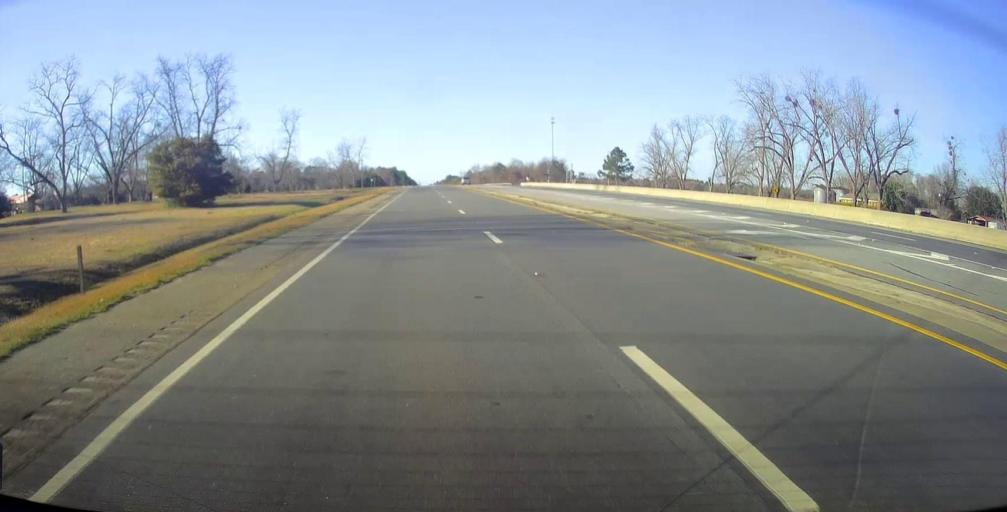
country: US
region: Georgia
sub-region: Lee County
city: Leesburg
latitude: 31.8222
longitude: -84.2148
